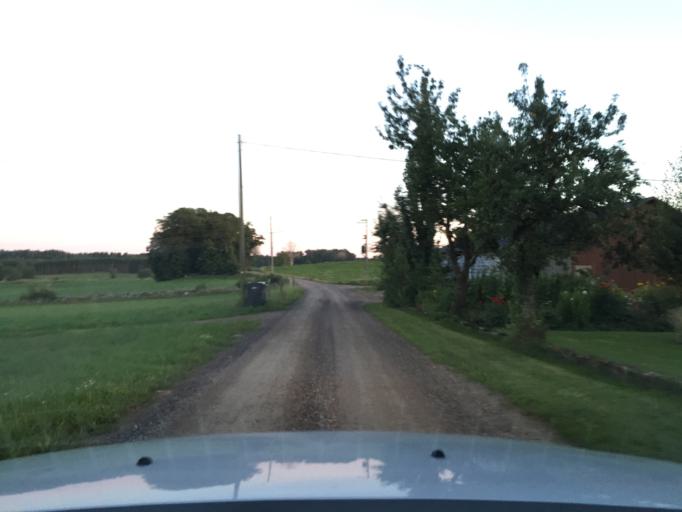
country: SE
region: Skane
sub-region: Hassleholms Kommun
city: Sosdala
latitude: 55.9838
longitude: 13.6784
